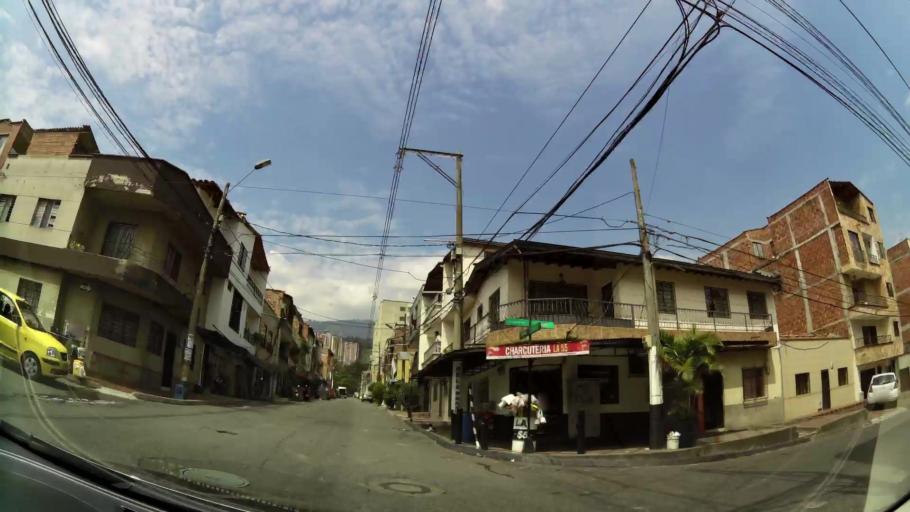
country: CO
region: Antioquia
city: Bello
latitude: 6.3212
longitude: -75.5605
